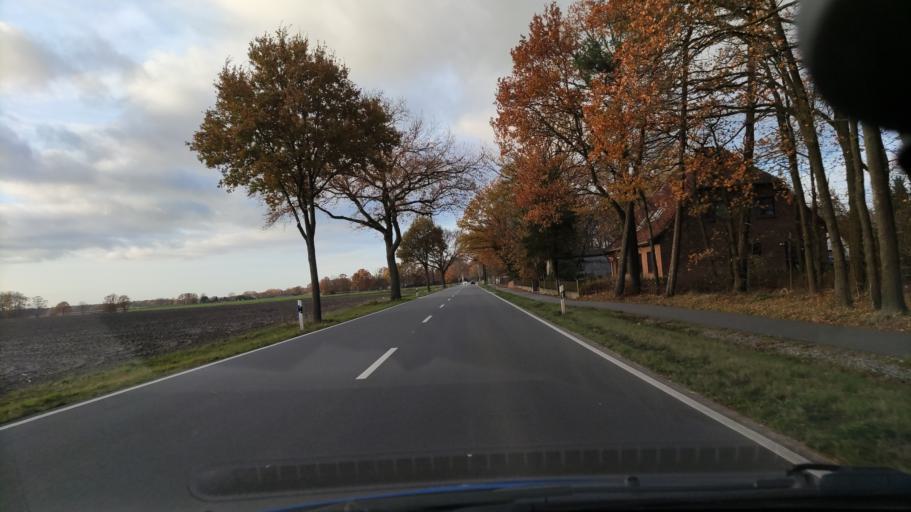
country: DE
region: Lower Saxony
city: Neuenkirchen
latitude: 53.0406
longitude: 9.6977
